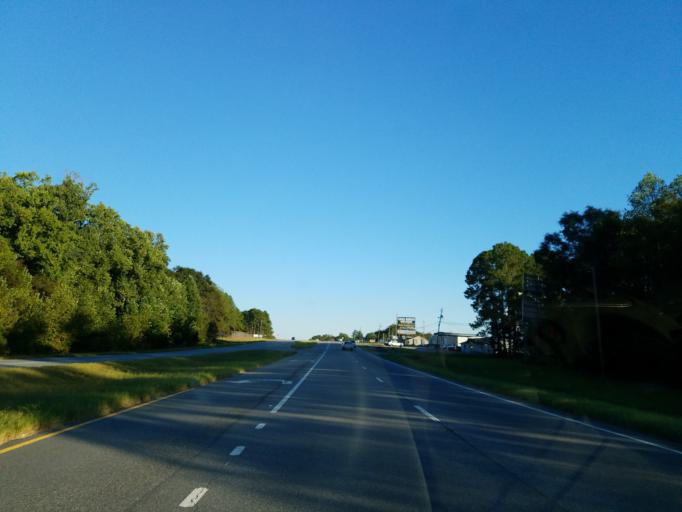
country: US
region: Georgia
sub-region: Worth County
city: Sylvester
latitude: 31.5209
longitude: -83.7885
